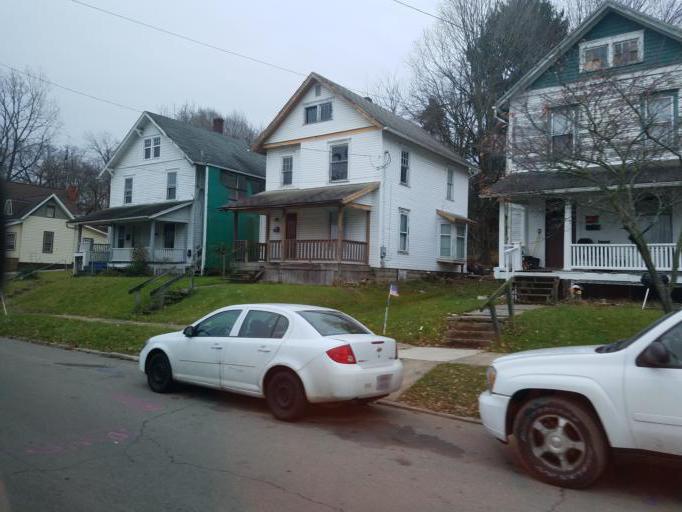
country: US
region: Ohio
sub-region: Richland County
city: Mansfield
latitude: 40.7558
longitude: -82.5073
